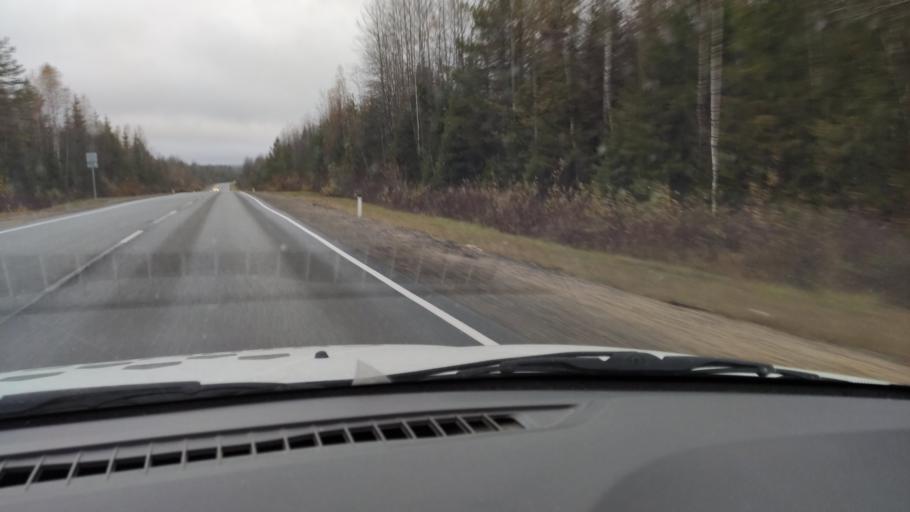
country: RU
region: Kirov
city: Omutninsk
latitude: 58.7035
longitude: 52.1088
